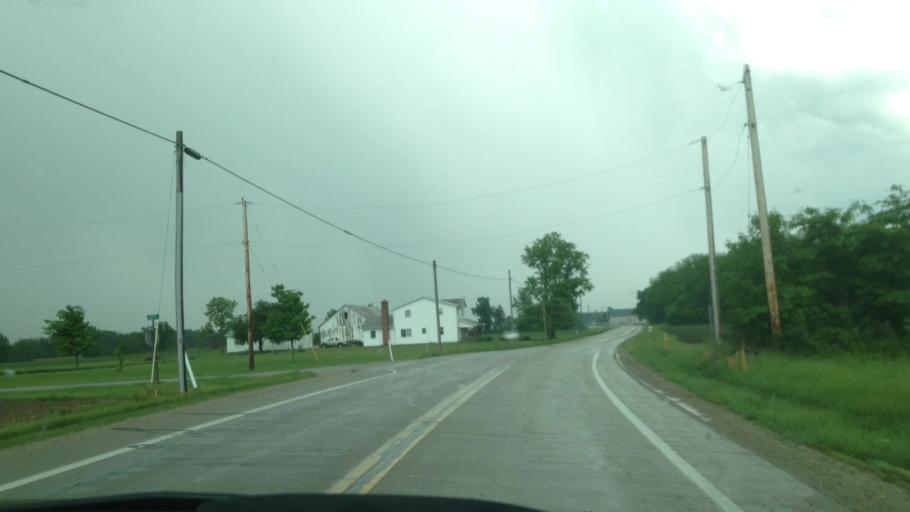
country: US
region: Ohio
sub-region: Darke County
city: Greenville
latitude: 40.1508
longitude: -84.6641
